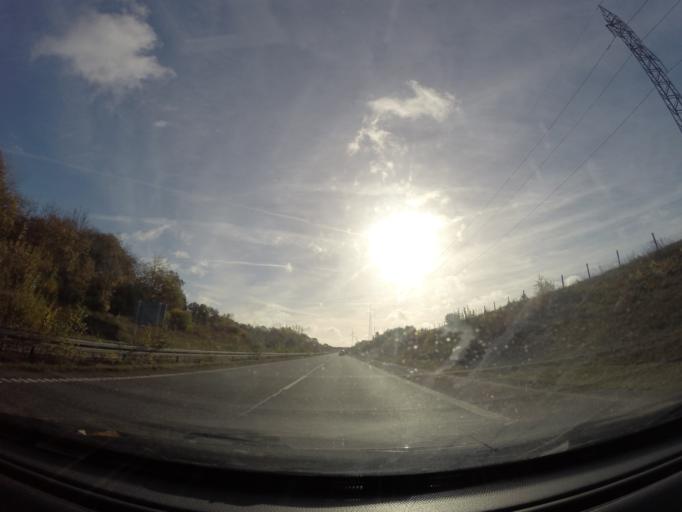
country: DK
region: South Denmark
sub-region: Svendborg Kommune
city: Svendborg
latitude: 55.1052
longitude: 10.5646
